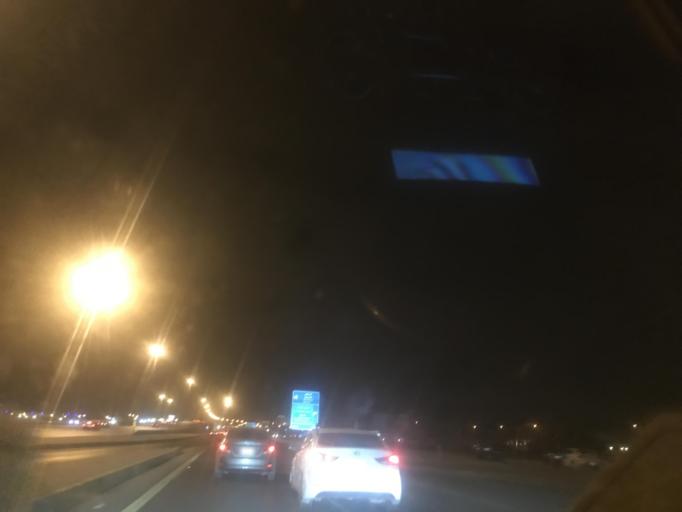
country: SA
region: Ar Riyad
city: Riyadh
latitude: 24.7699
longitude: 46.5751
